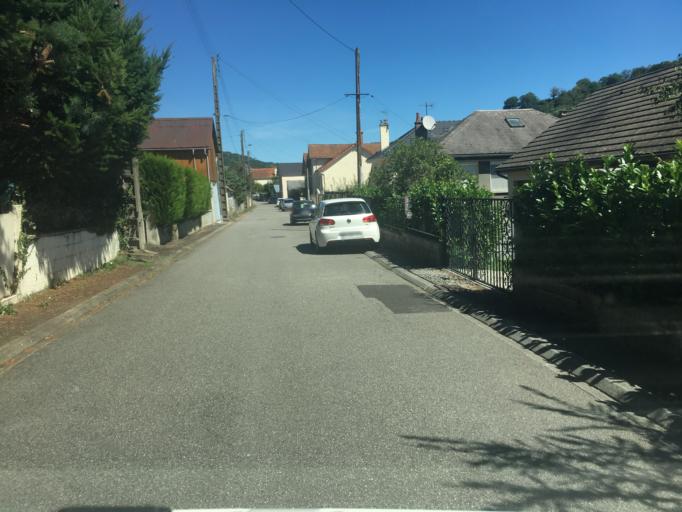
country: FR
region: Limousin
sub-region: Departement de la Correze
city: Bort-les-Orgues
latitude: 45.3967
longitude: 2.4960
